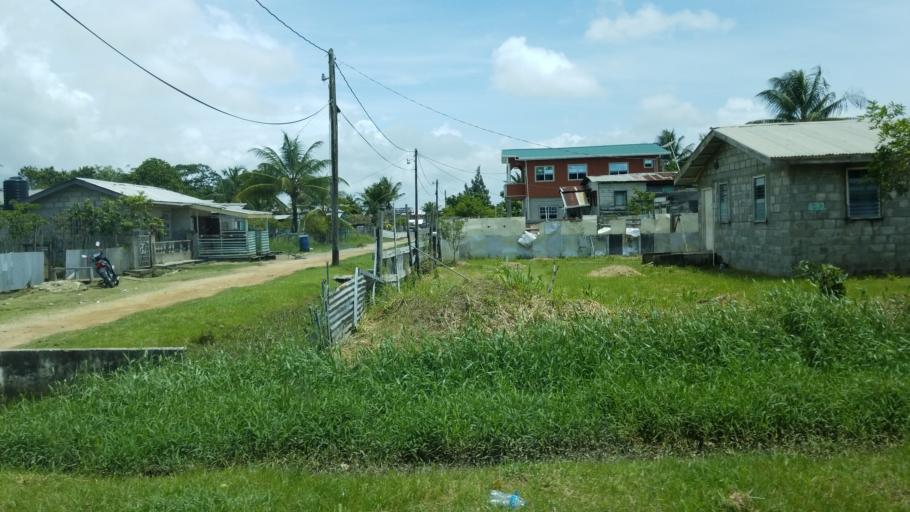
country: GY
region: Demerara-Mahaica
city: Georgetown
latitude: 6.7935
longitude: -58.1201
